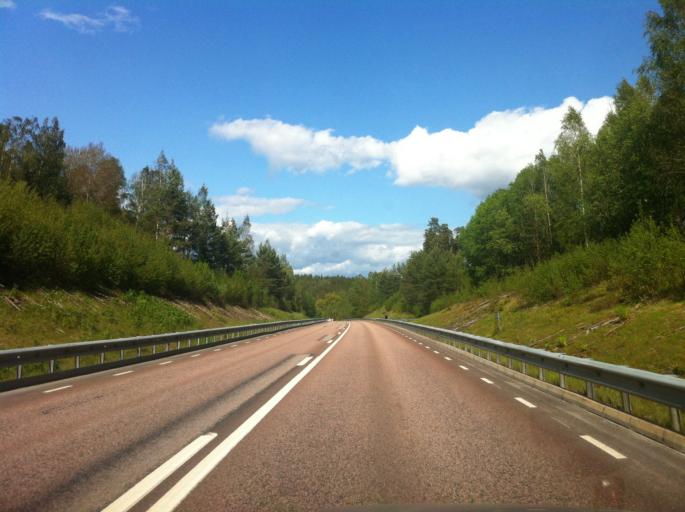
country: SE
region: Vaermland
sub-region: Kristinehamns Kommun
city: Kristinehamn
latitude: 59.3913
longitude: 14.1998
